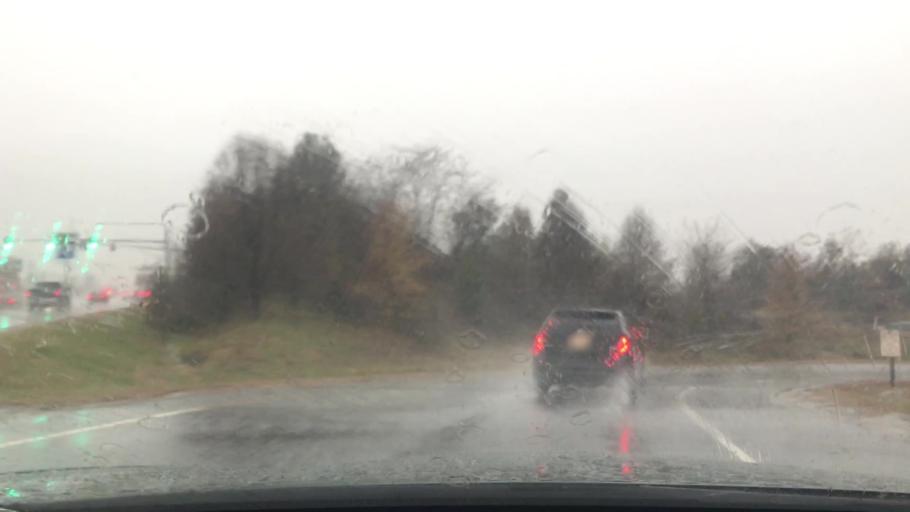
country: US
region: Virginia
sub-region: Stafford County
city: Aquia Harbour
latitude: 38.4661
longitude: -77.4088
